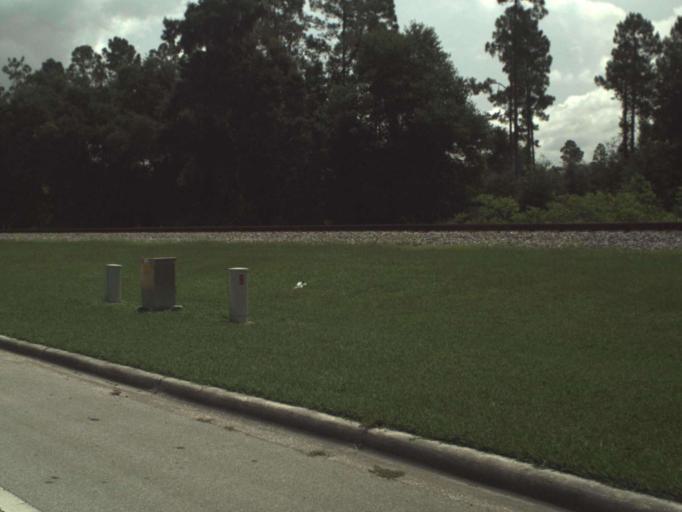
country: US
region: Florida
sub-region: Sumter County
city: Bushnell
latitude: 28.6552
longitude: -82.1162
